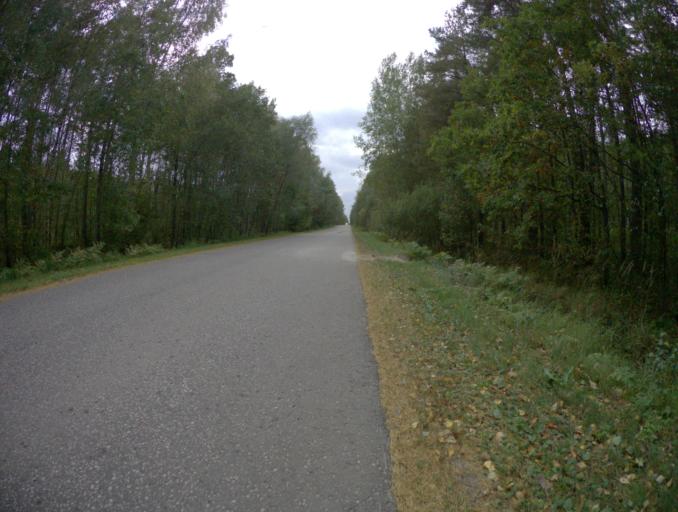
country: RU
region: Vladimir
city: Orgtrud
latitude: 56.1525
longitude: 40.5742
